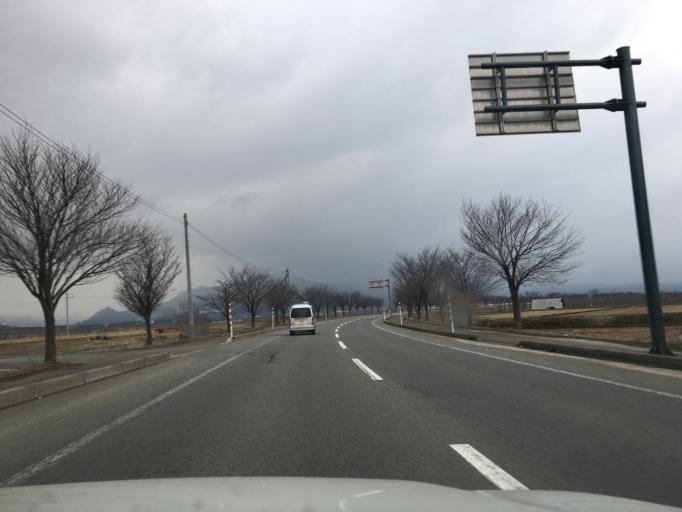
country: JP
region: Aomori
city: Kuroishi
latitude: 40.5706
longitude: 140.5670
